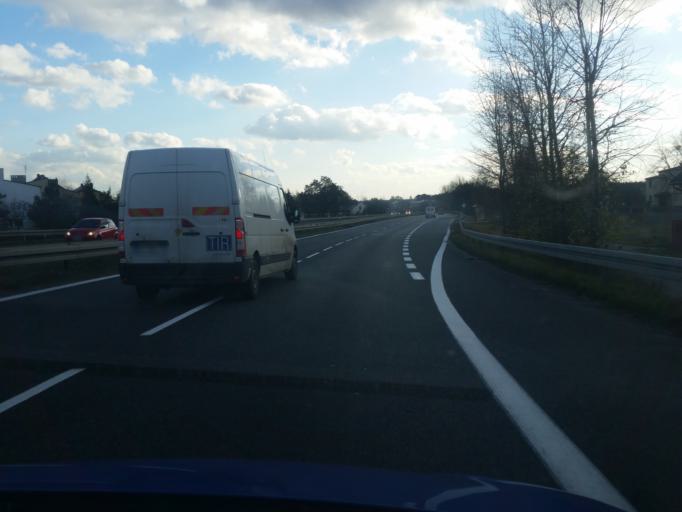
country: PL
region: Silesian Voivodeship
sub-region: Powiat bedzinski
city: Siewierz
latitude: 50.4757
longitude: 19.2283
